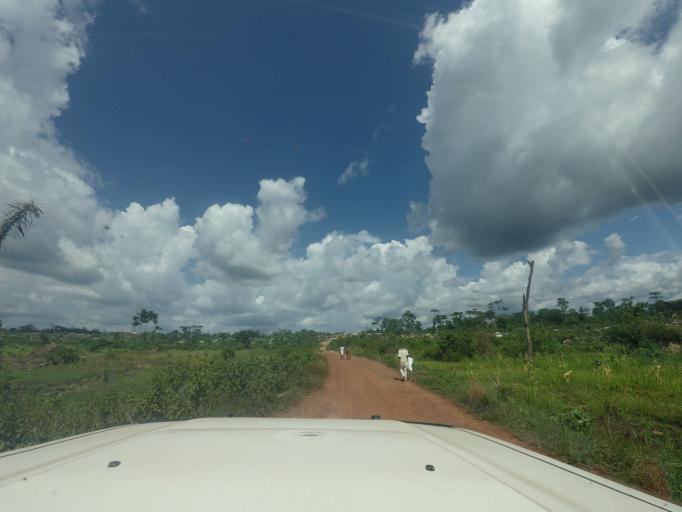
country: LR
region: Grand Gedeh
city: Zwedru
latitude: 6.0313
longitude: -8.0536
